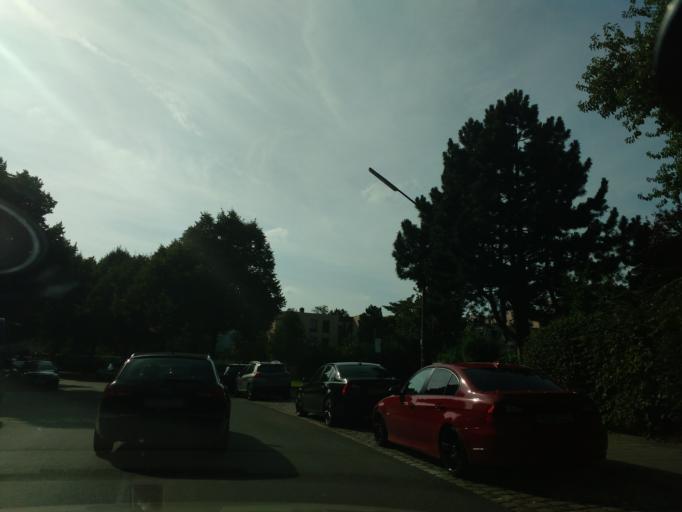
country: DE
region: Bavaria
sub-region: Upper Bavaria
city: Pasing
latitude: 48.1528
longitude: 11.4381
